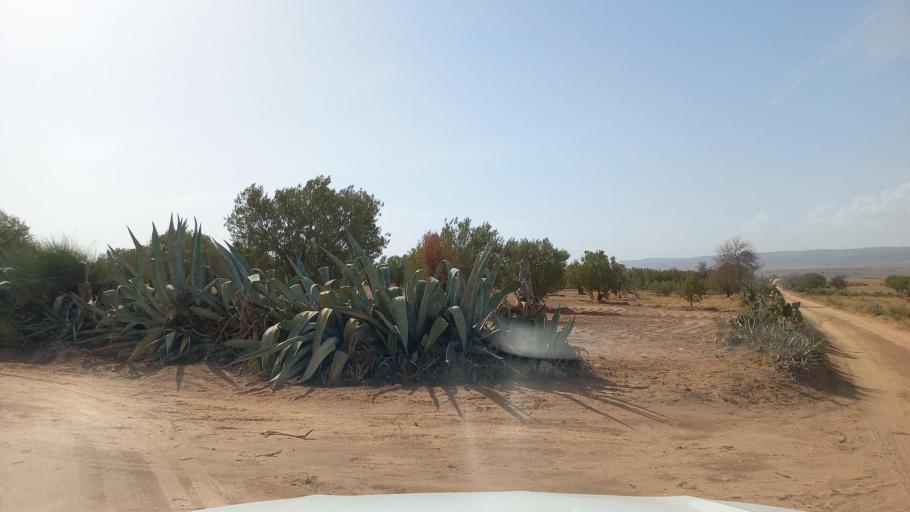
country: TN
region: Al Qasrayn
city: Kasserine
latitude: 35.2111
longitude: 8.9790
